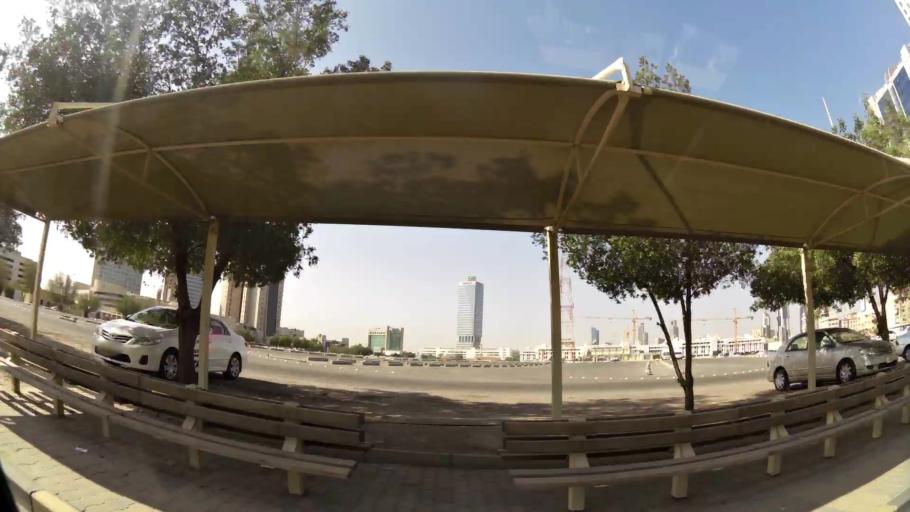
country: KW
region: Al Asimah
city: Kuwait City
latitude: 29.3665
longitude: 47.9821
